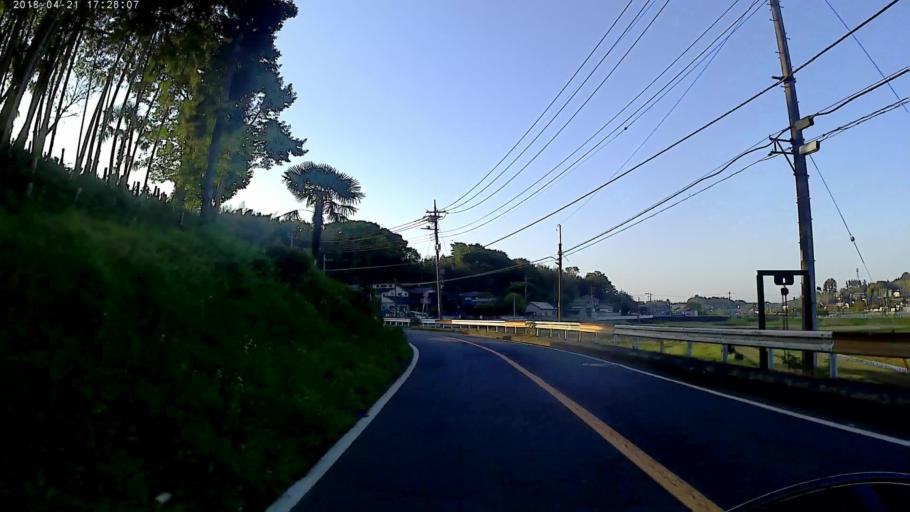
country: JP
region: Kanagawa
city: Atsugi
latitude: 35.4208
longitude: 139.4131
